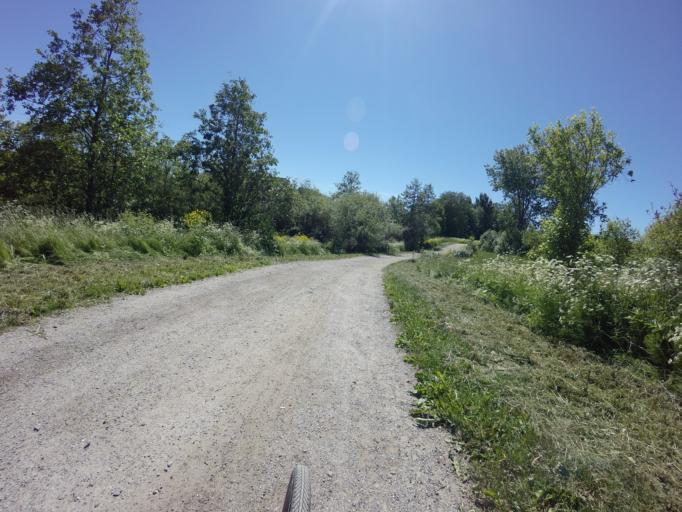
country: FI
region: Varsinais-Suomi
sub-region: Turku
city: Turku
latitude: 60.4625
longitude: 22.2800
